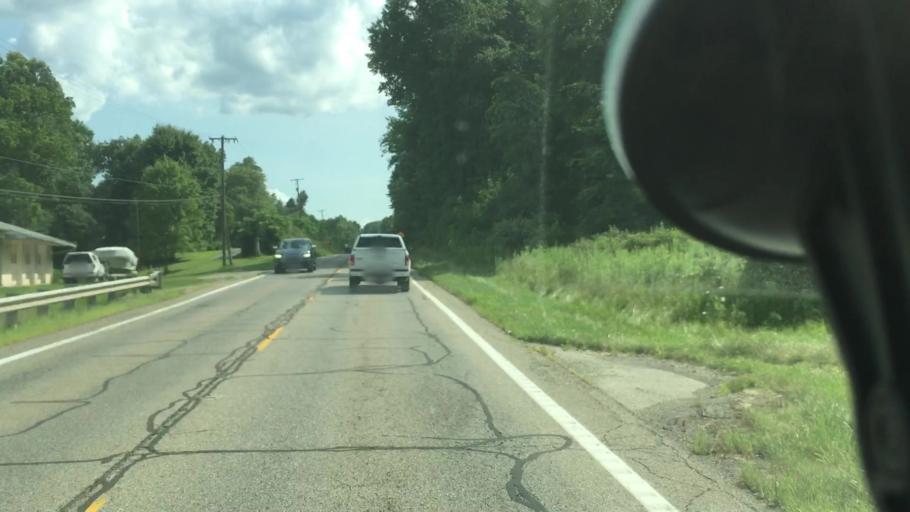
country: US
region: Ohio
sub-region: Columbiana County
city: Salem
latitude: 40.9477
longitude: -80.8356
